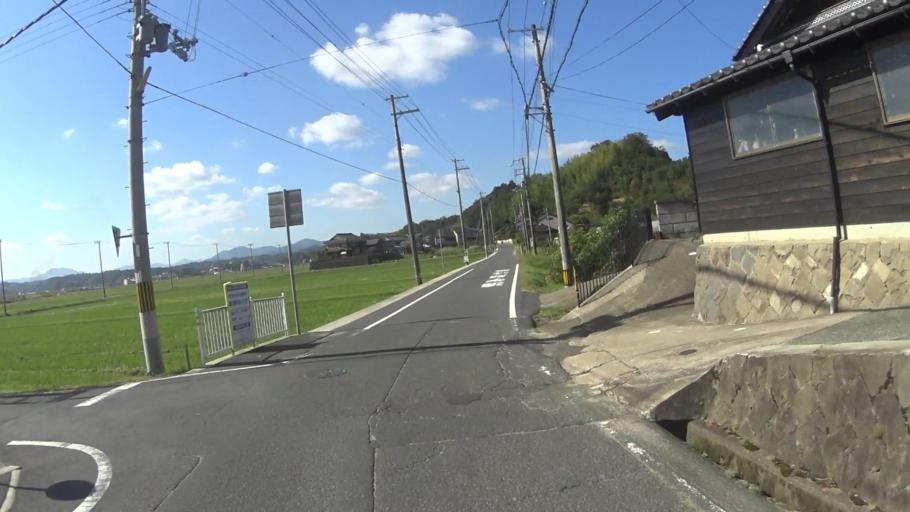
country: JP
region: Kyoto
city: Miyazu
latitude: 35.6812
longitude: 135.0905
